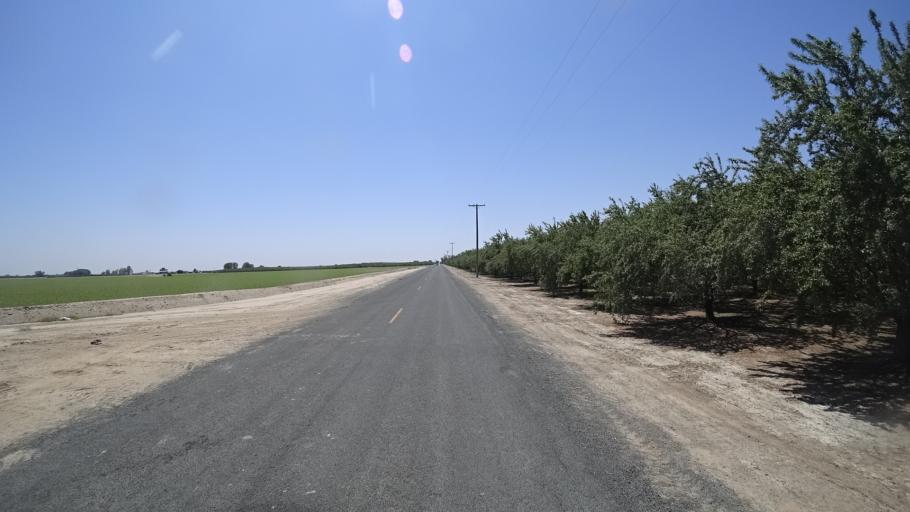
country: US
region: California
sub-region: Kings County
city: Armona
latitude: 36.2672
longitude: -119.7269
